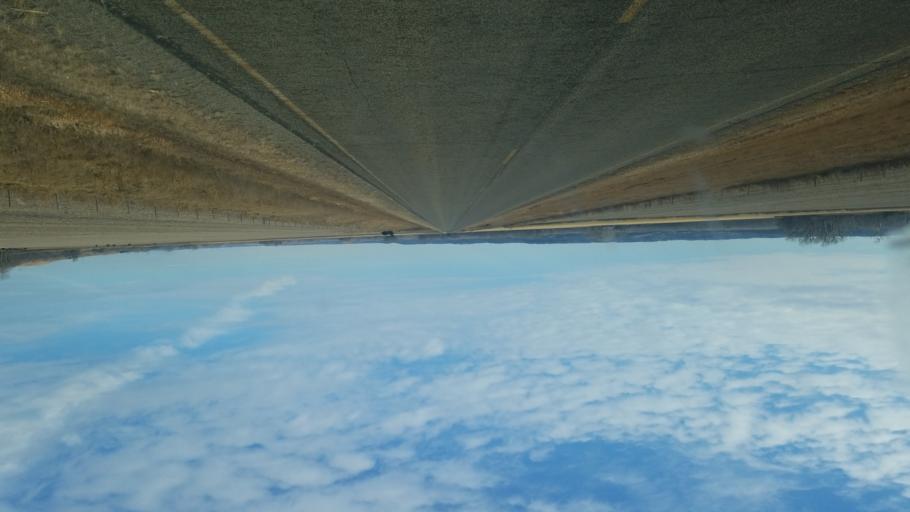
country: US
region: South Dakota
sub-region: Charles Mix County
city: Wagner
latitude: 42.8927
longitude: -98.2810
